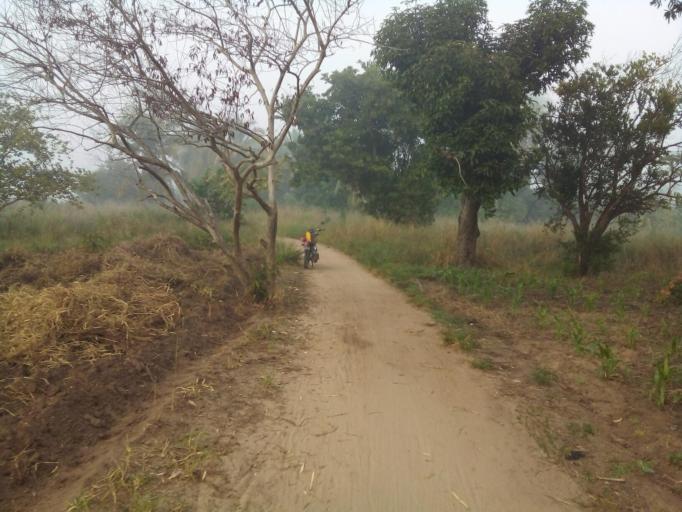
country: MZ
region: Zambezia
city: Quelimane
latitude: -17.5882
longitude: 36.6874
